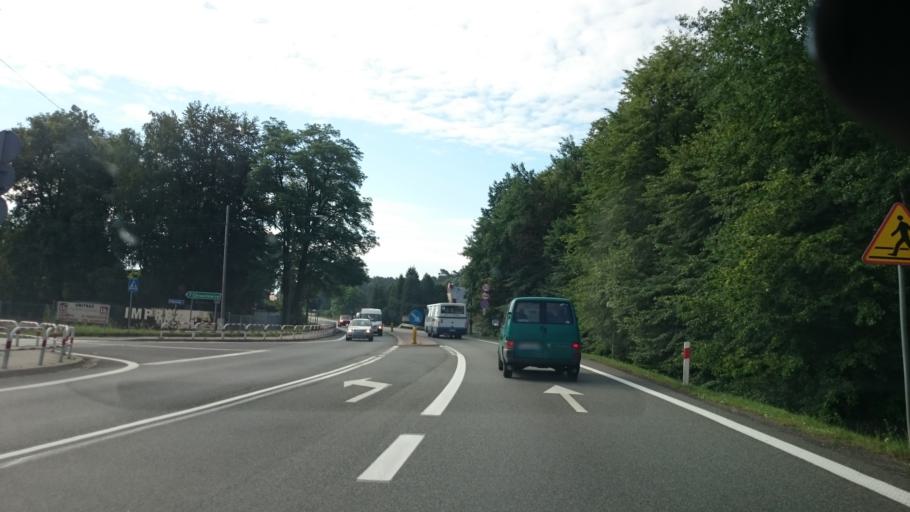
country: PL
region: Opole Voivodeship
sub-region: Powiat opolski
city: Tarnow Opolski
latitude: 50.6050
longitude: 18.0750
